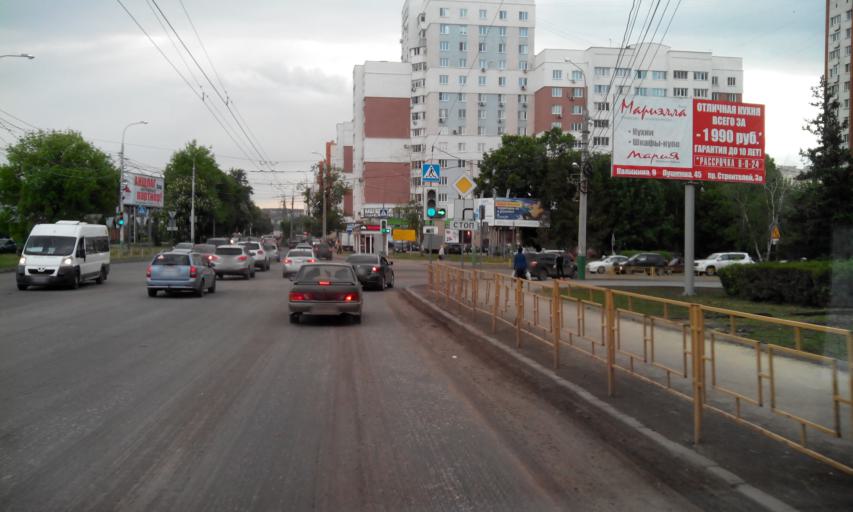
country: RU
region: Penza
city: Penza
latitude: 53.1974
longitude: 44.9994
